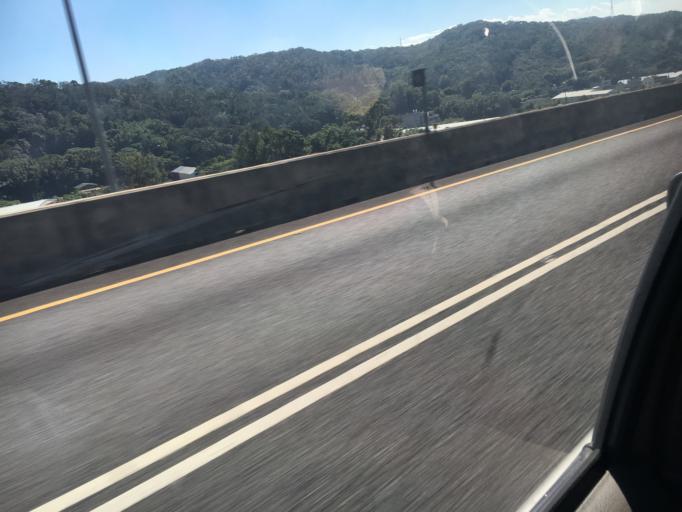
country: TW
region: Taiwan
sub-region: Taoyuan
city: Taoyuan
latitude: 25.0559
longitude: 121.3280
